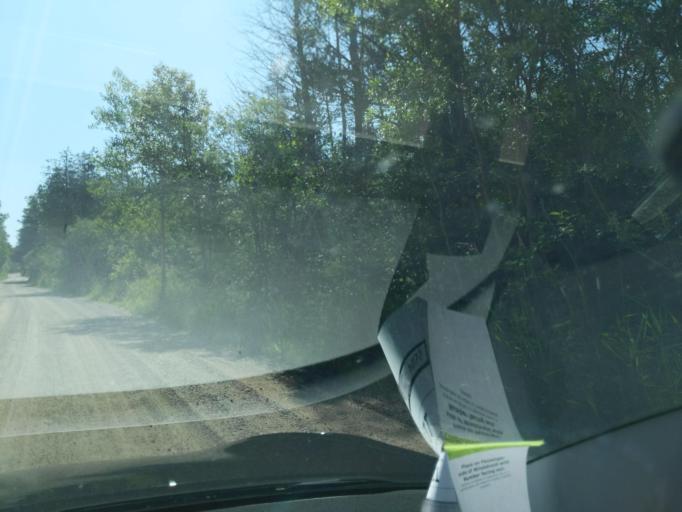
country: US
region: Michigan
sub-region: Mackinac County
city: Saint Ignace
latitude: 45.6794
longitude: -84.6953
